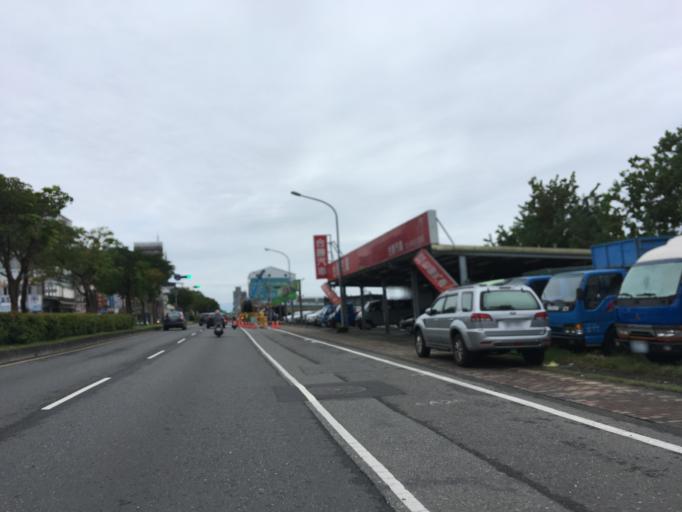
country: TW
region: Taiwan
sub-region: Yilan
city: Yilan
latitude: 24.7002
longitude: 121.7694
